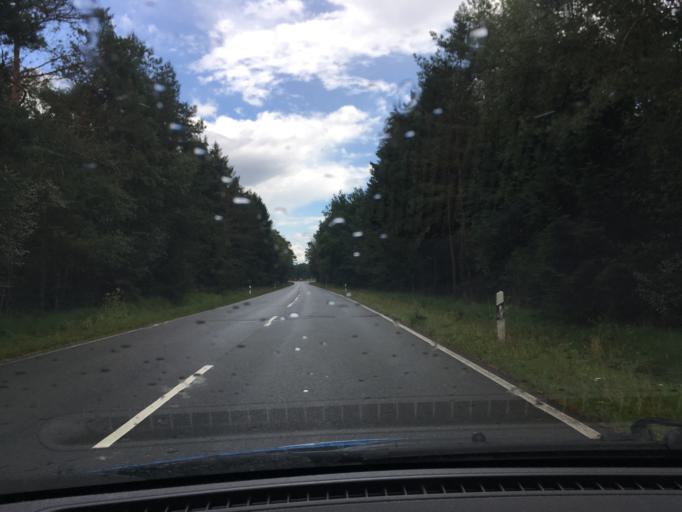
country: DE
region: Lower Saxony
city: Wietzendorf
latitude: 52.9686
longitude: 9.9539
